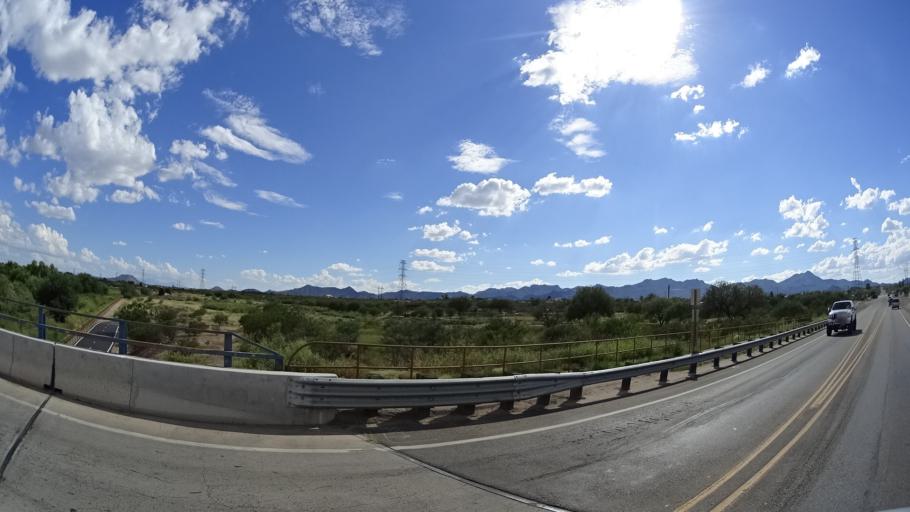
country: US
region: Arizona
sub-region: Pima County
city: Flowing Wells
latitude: 32.2943
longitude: -111.0386
